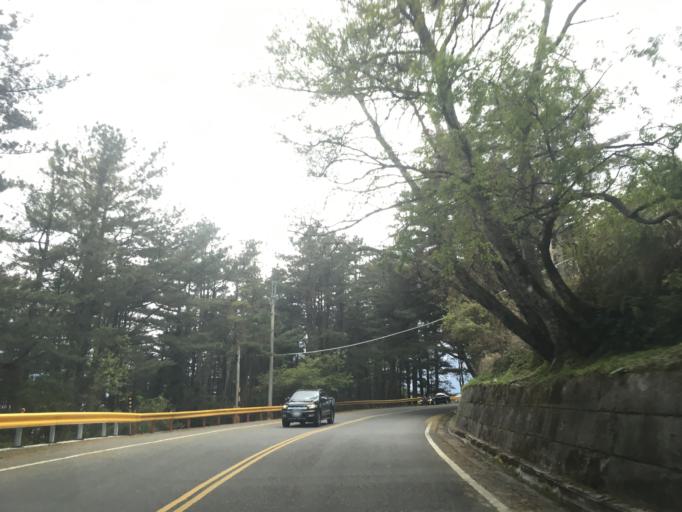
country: TW
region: Taiwan
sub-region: Hualien
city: Hualian
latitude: 24.1830
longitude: 121.3267
